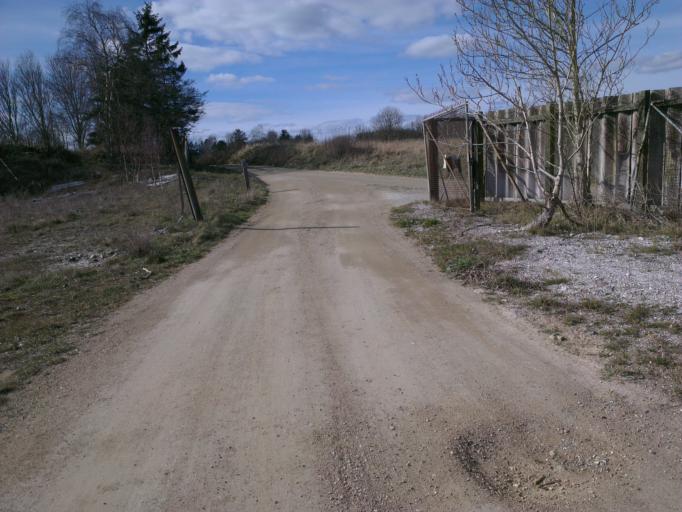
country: DK
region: Zealand
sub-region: Roskilde Kommune
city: Jyllinge
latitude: 55.7517
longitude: 12.0609
